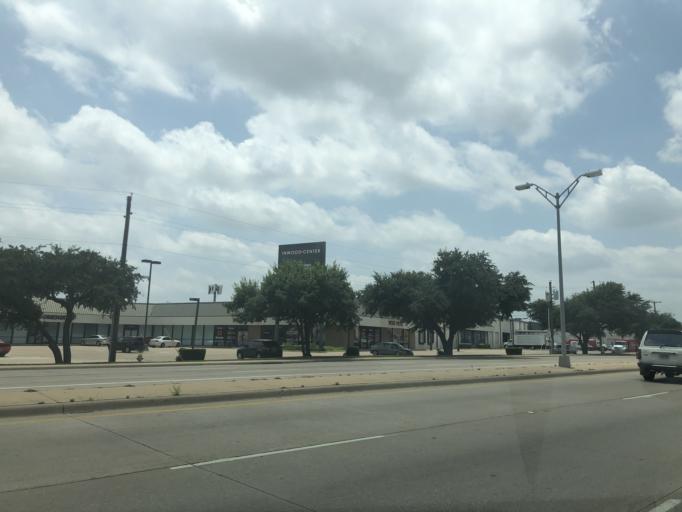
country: US
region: Texas
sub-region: Dallas County
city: Dallas
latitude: 32.8060
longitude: -96.8528
